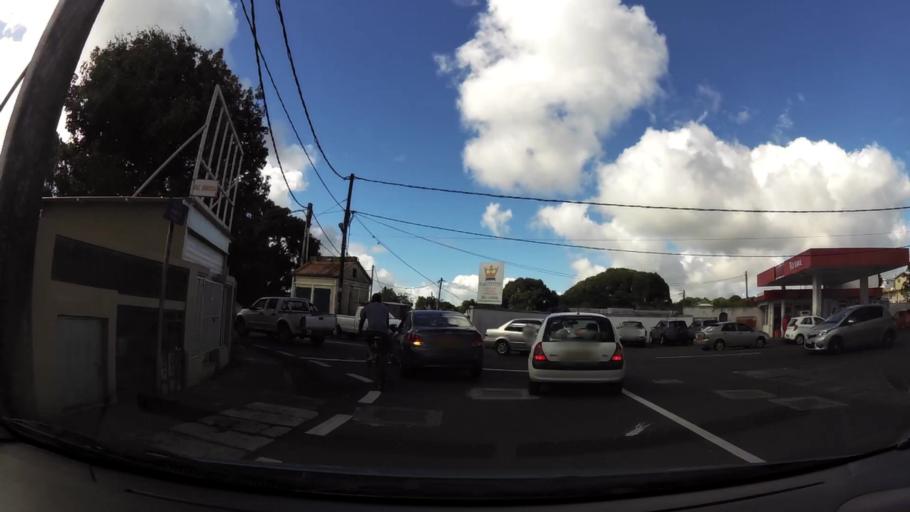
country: MU
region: Plaines Wilhems
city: Curepipe
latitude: -20.3270
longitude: 57.5286
